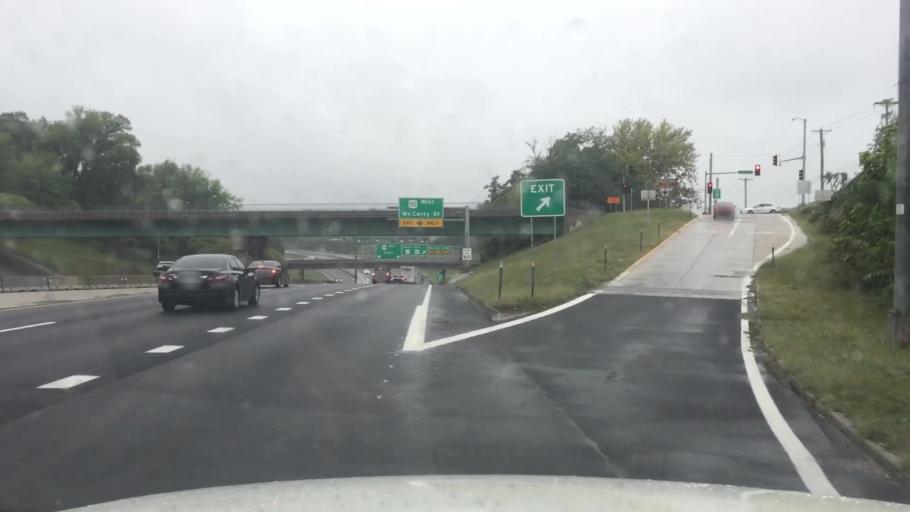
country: US
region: Missouri
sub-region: Cole County
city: Jefferson City
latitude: 38.5858
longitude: -92.1806
